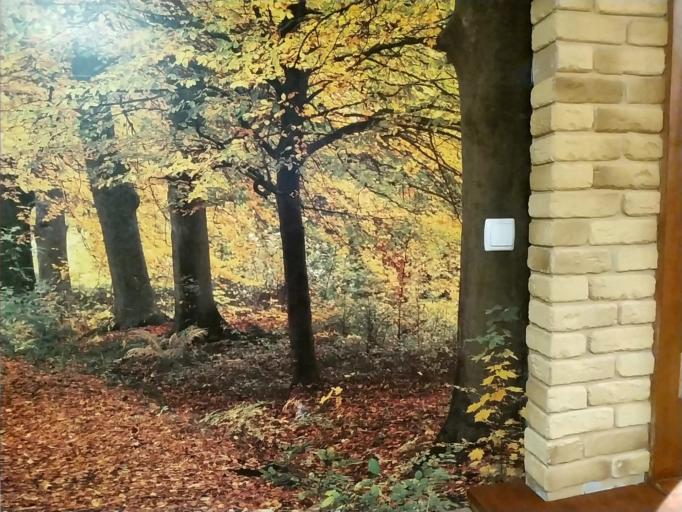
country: RU
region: Smolensk
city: Safonovo
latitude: 55.2003
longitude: 33.2093
